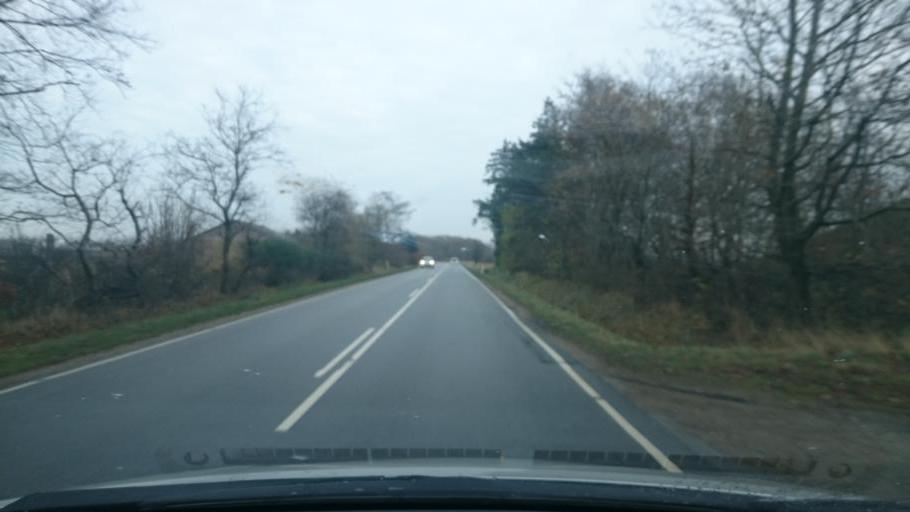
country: DK
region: South Denmark
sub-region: Esbjerg Kommune
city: Ribe
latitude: 55.3343
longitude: 8.8250
